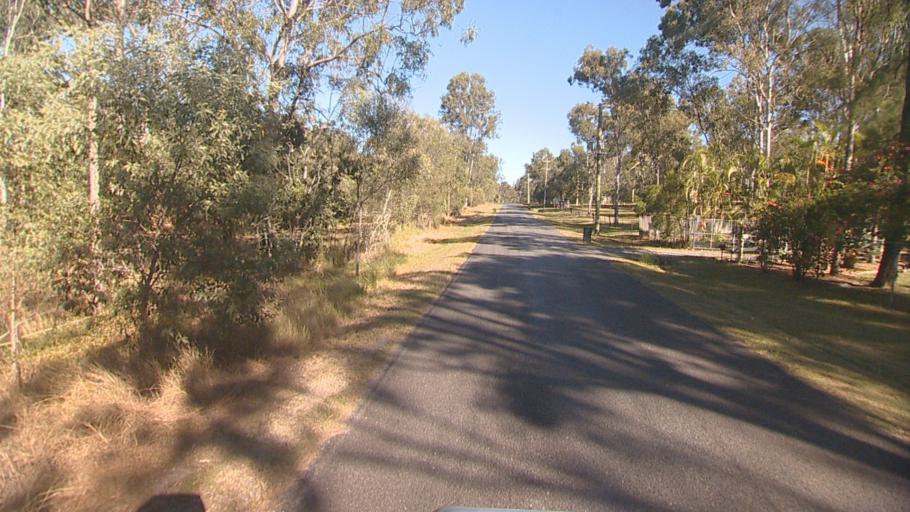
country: AU
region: Queensland
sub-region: Logan
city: Park Ridge South
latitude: -27.7245
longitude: 152.9908
